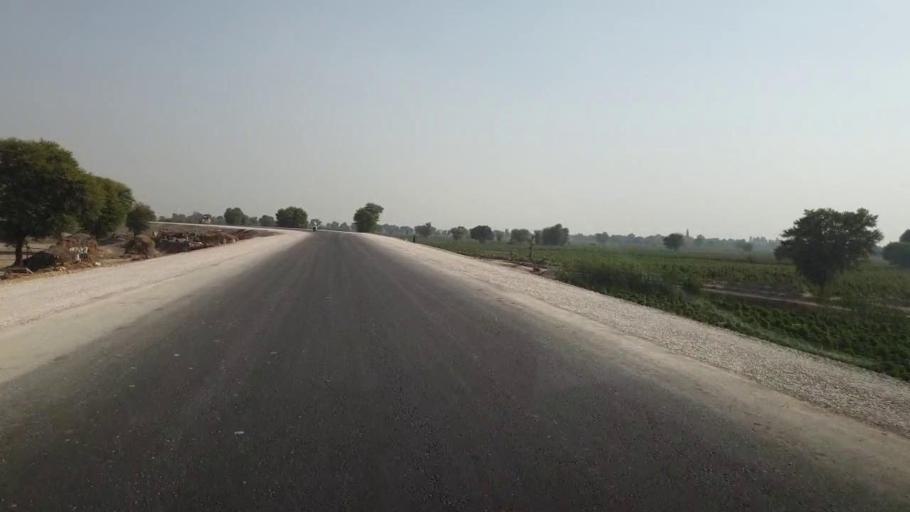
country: PK
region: Sindh
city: Bhan
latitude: 26.5535
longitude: 67.7787
